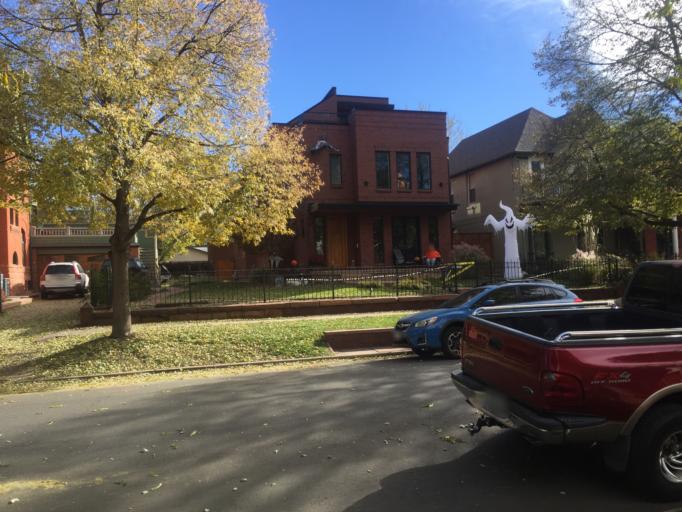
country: US
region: Colorado
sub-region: Denver County
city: Denver
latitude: 39.7491
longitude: -104.9757
